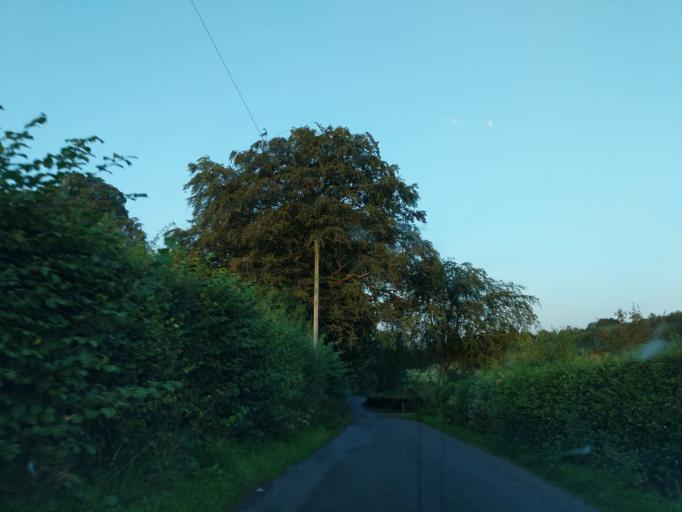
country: GB
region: Scotland
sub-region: Stirling
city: Doune
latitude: 56.1230
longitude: -4.0724
